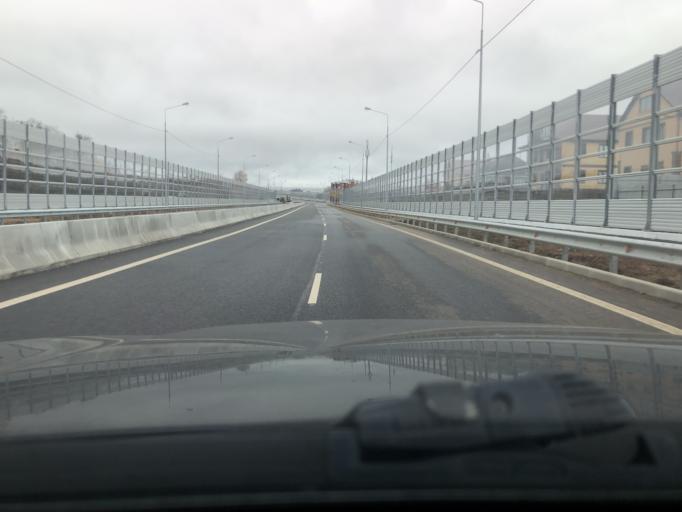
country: RU
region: Moskovskaya
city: Sergiyev Posad
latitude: 56.3044
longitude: 38.1014
